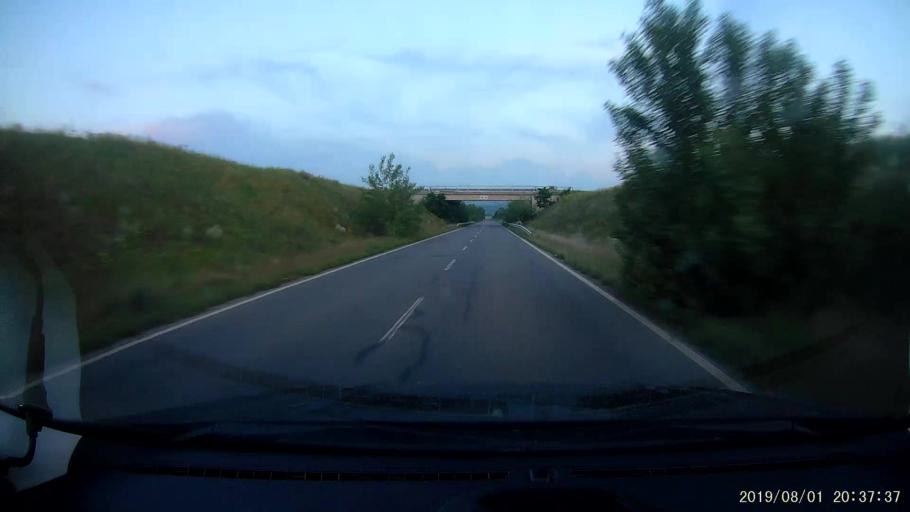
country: BG
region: Yambol
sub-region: Obshtina Elkhovo
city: Elkhovo
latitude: 42.0441
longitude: 26.5950
